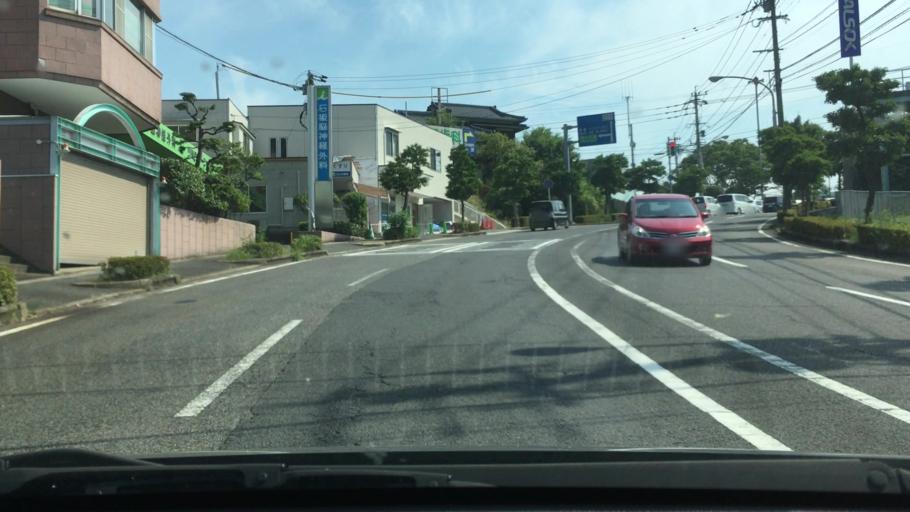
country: JP
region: Nagasaki
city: Sasebo
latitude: 33.1527
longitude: 129.7714
